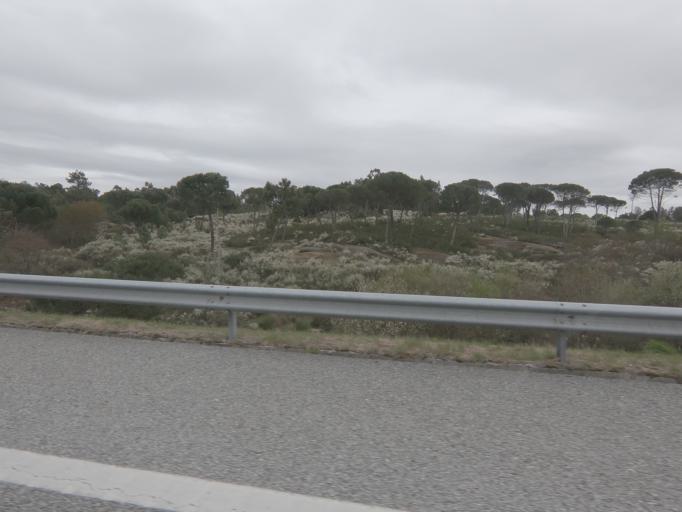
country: PT
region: Viseu
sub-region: Viseu
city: Viseu
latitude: 40.6286
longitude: -7.8969
